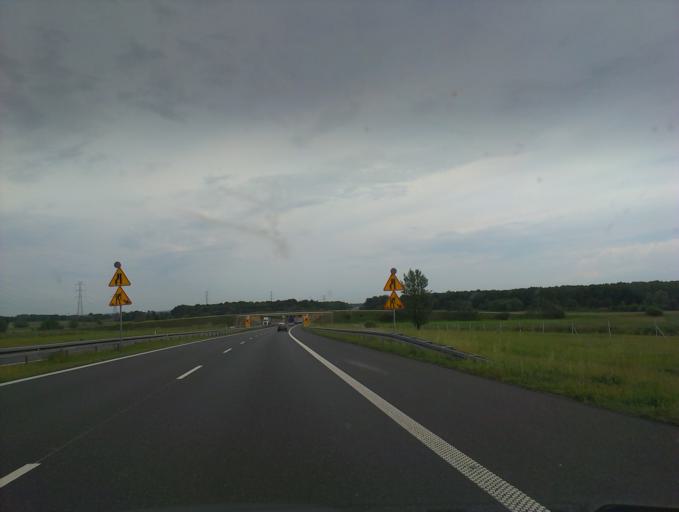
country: PL
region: Opole Voivodeship
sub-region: Powiat brzeski
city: Olszanka
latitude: 50.7345
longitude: 17.4953
